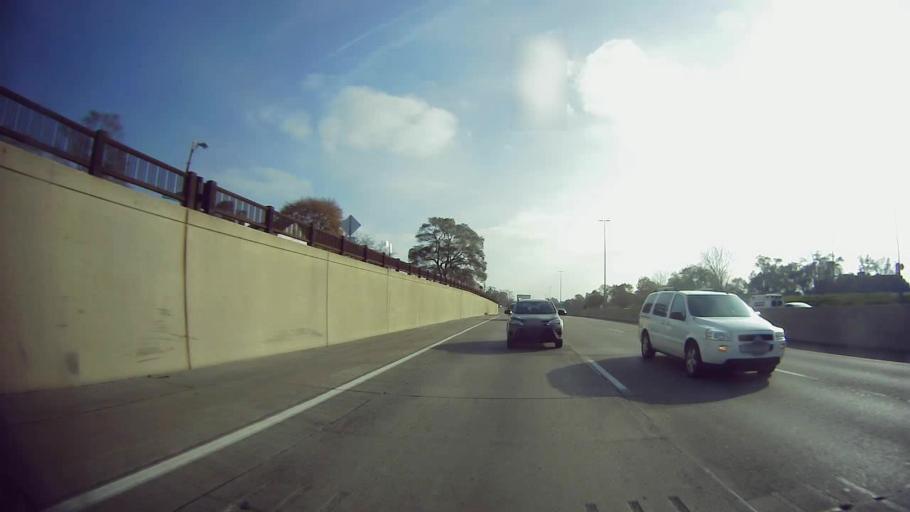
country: US
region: Michigan
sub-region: Wayne County
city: Highland Park
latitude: 42.3903
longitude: -83.1038
